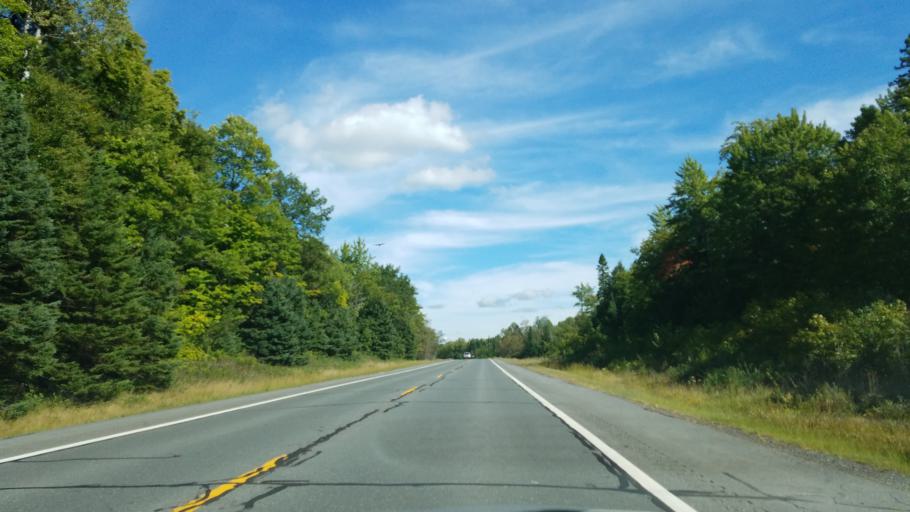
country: US
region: Michigan
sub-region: Baraga County
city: L'Anse
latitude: 46.5799
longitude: -88.4559
